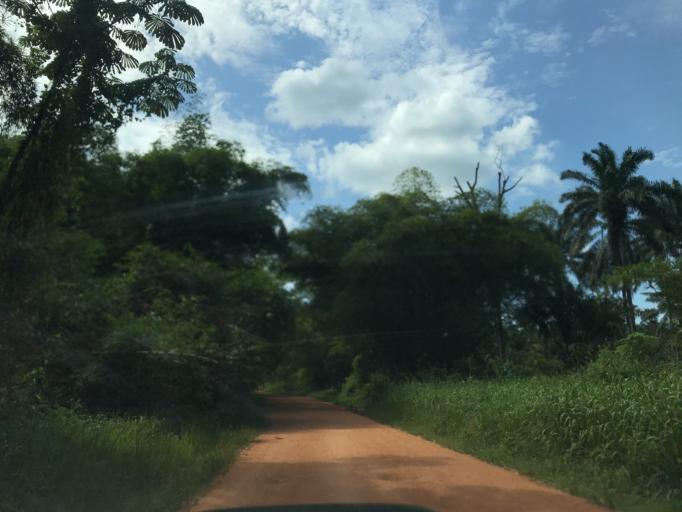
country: CD
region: Eastern Province
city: Kisangani
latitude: 1.0581
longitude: 25.2749
